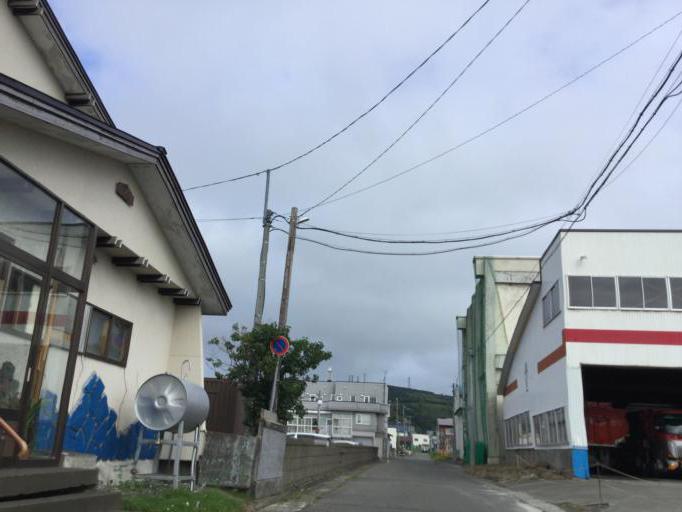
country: JP
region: Hokkaido
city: Wakkanai
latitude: 45.4007
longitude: 141.6840
